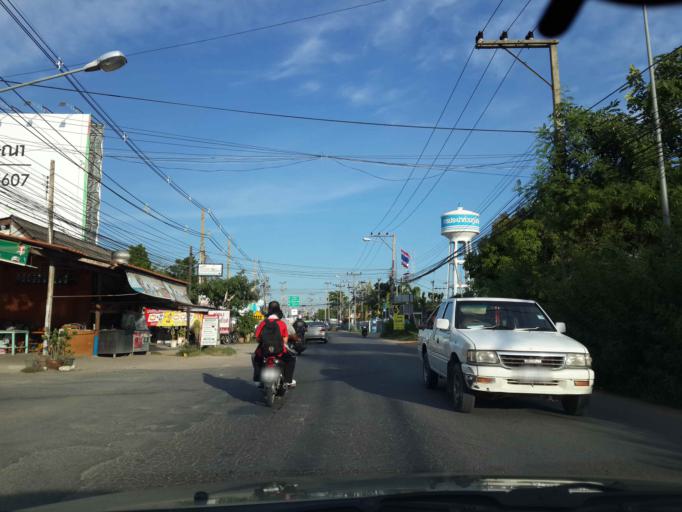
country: TH
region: Chon Buri
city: Phatthaya
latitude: 12.9642
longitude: 100.9191
